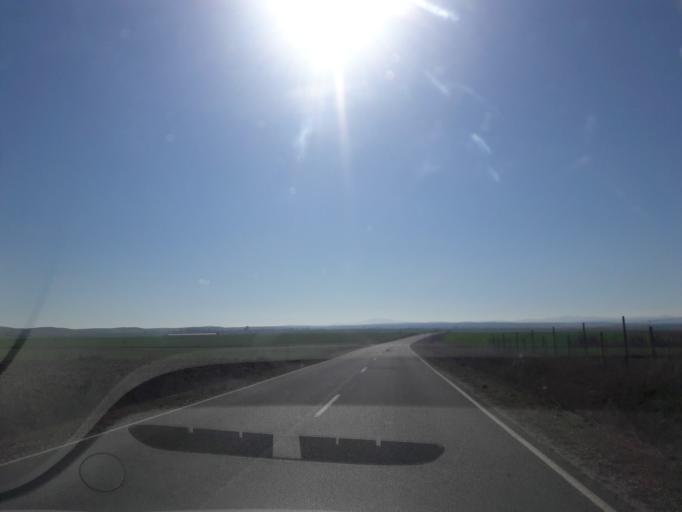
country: ES
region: Castille and Leon
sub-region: Provincia de Salamanca
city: Santiago de la Puebla
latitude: 40.8137
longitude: -5.2564
